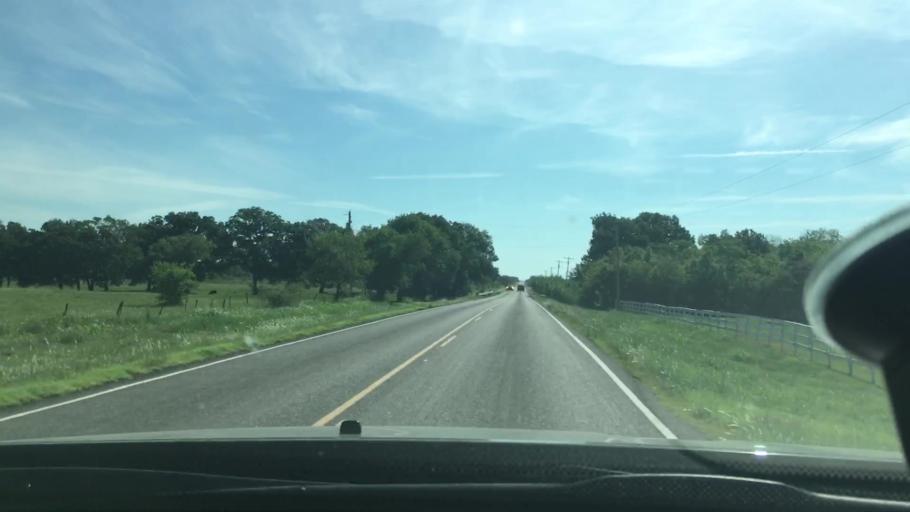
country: US
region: Oklahoma
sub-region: Carter County
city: Lone Grove
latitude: 34.3327
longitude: -97.2053
